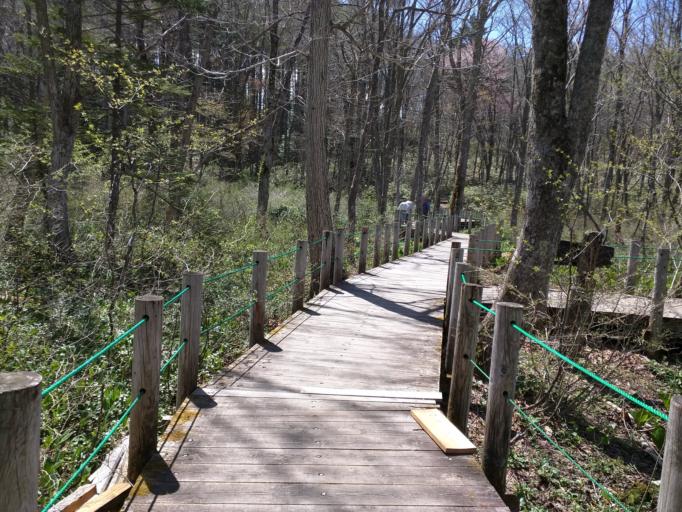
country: JP
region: Nagano
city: Nagano-shi
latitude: 36.7554
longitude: 138.0717
